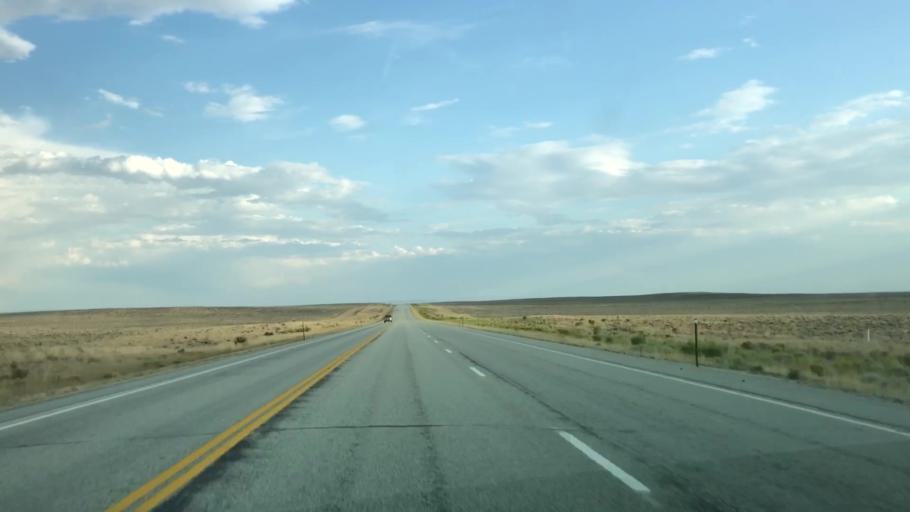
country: US
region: Wyoming
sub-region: Sweetwater County
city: North Rock Springs
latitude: 42.2734
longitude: -109.4808
